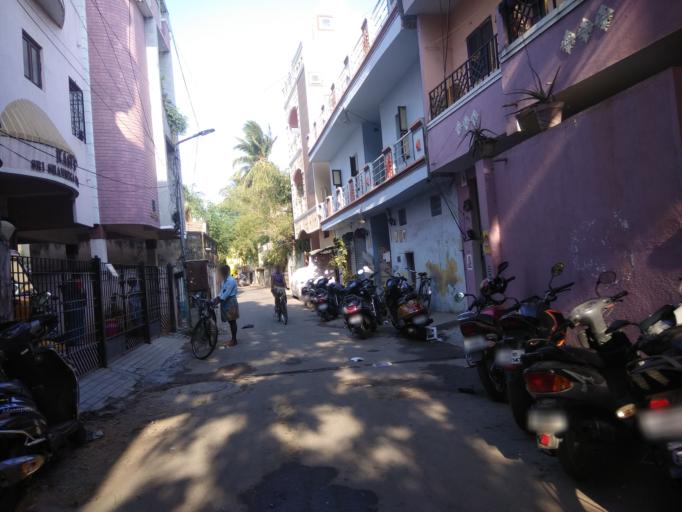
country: IN
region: Tamil Nadu
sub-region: Chennai
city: Chetput
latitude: 13.0591
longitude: 80.2229
